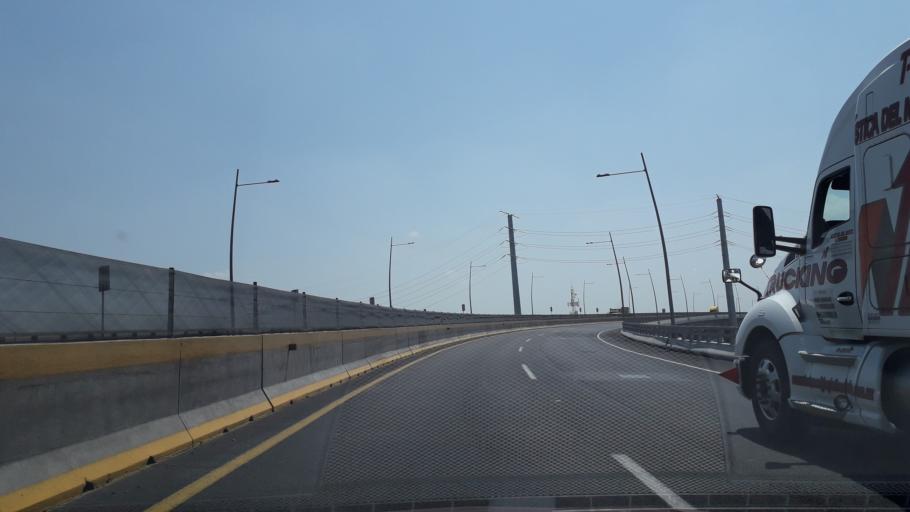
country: MX
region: Puebla
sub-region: Puebla
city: San Sebastian de Aparicio
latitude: 19.0826
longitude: -98.1665
